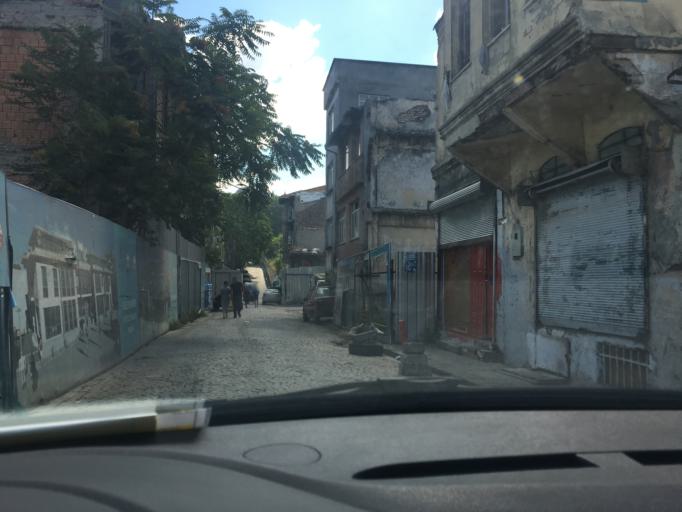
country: TR
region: Istanbul
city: Istanbul
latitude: 41.0171
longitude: 28.9607
